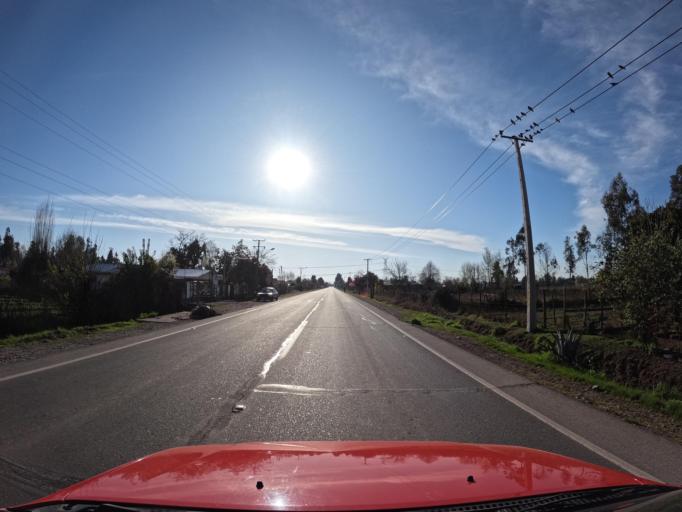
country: CL
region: Maule
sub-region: Provincia de Curico
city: Teno
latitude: -34.9471
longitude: -70.9931
